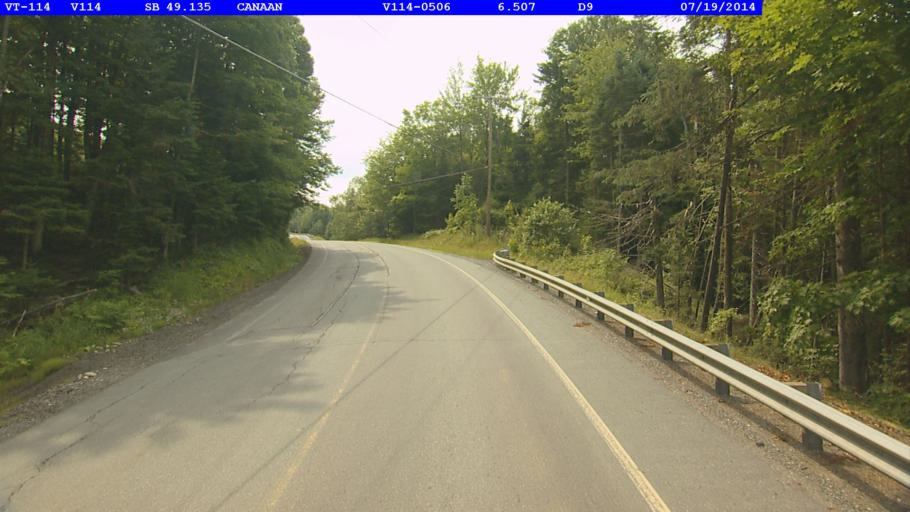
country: US
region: New Hampshire
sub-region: Coos County
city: Colebrook
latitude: 45.0097
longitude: -71.5656
